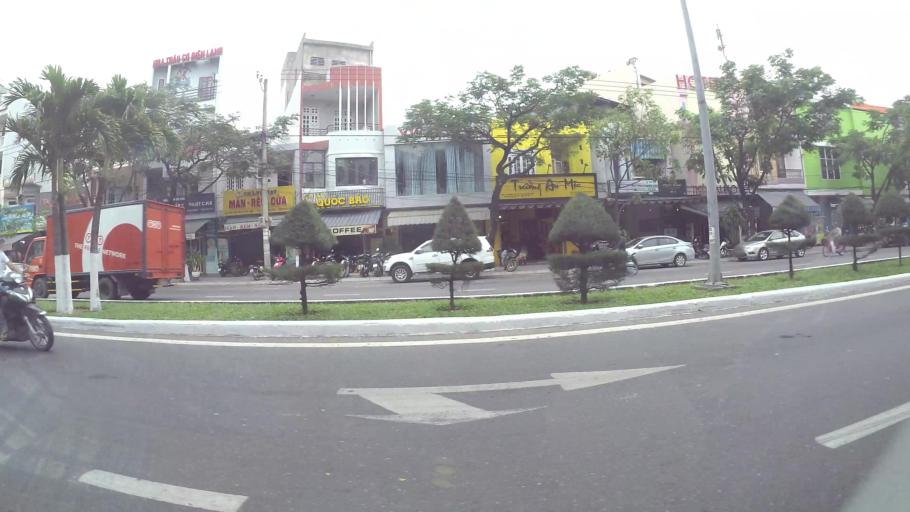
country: VN
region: Da Nang
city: Da Nang
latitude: 16.0463
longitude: 108.2096
